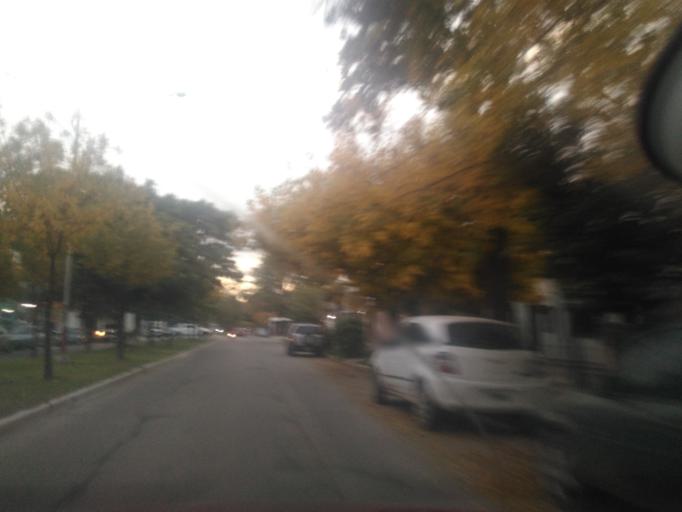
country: AR
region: Chaco
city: Resistencia
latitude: -27.4628
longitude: -58.9907
